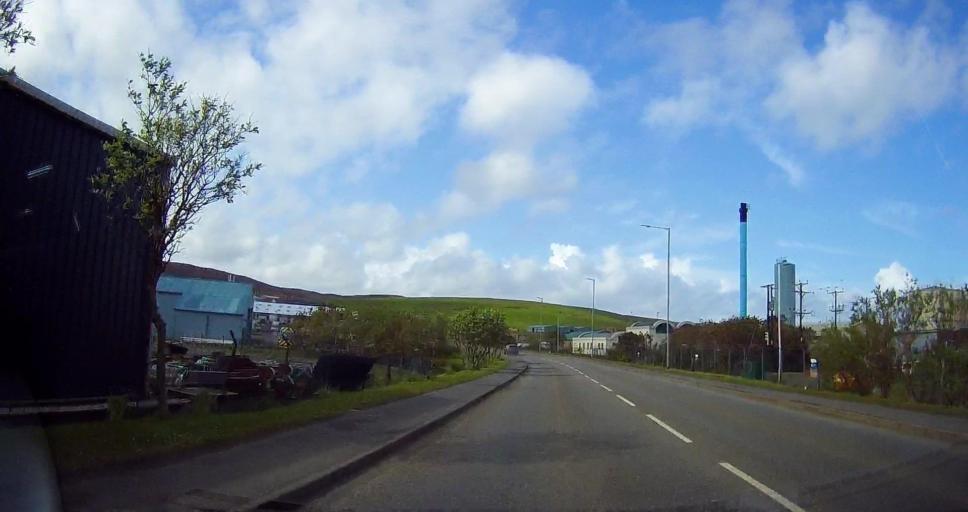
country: GB
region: Scotland
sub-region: Shetland Islands
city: Lerwick
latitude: 60.1670
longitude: -1.1650
